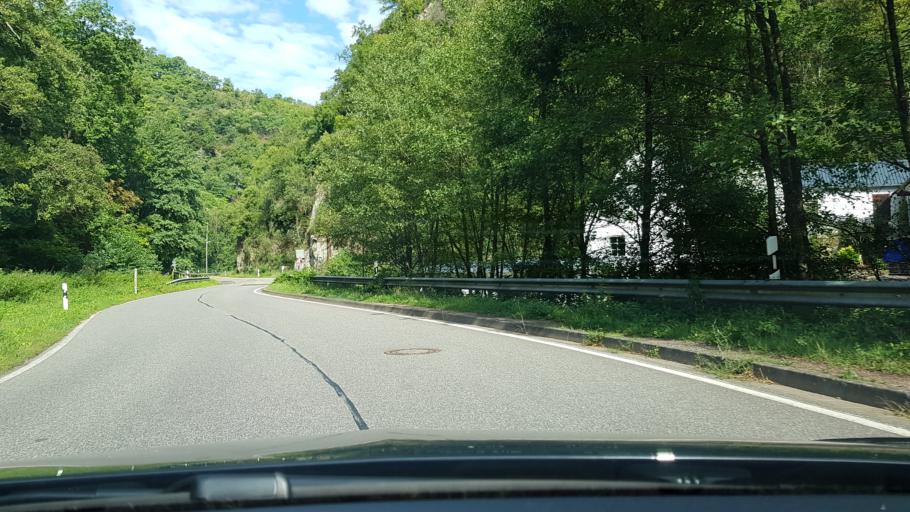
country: DE
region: Rheinland-Pfalz
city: Brodenbach
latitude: 50.2207
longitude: 7.4447
